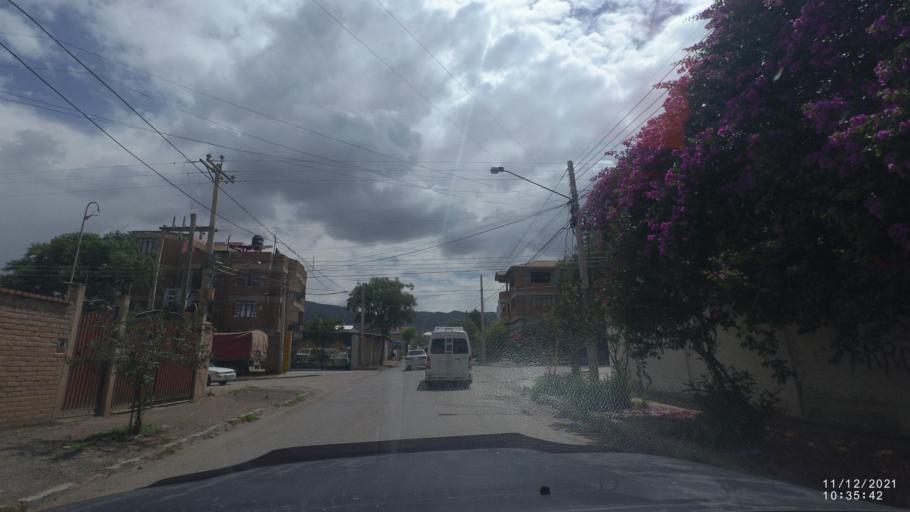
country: BO
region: Cochabamba
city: Cochabamba
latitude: -17.4509
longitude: -66.1269
